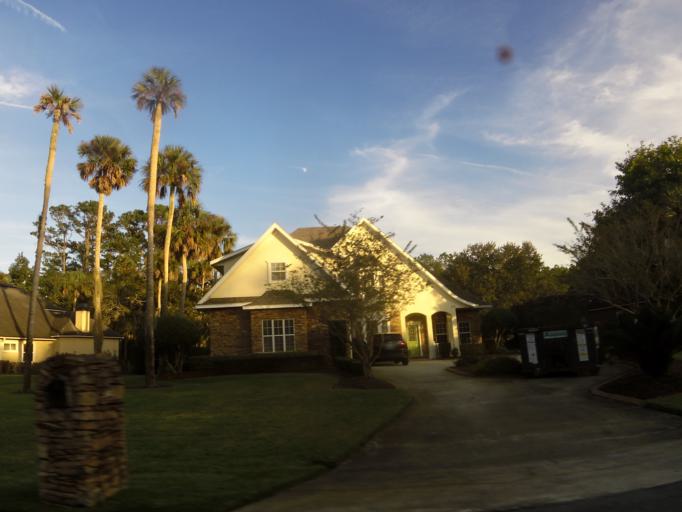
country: US
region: Florida
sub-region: Saint Johns County
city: Palm Valley
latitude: 30.1795
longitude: -81.3911
